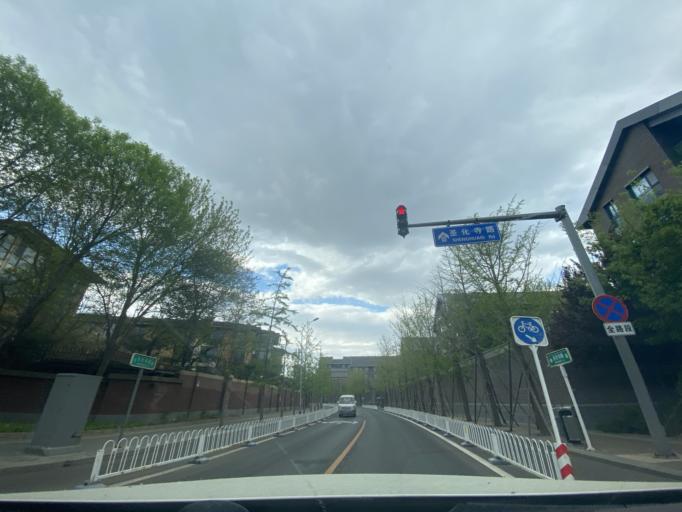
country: CN
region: Beijing
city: Haidian
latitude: 39.9706
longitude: 116.2862
